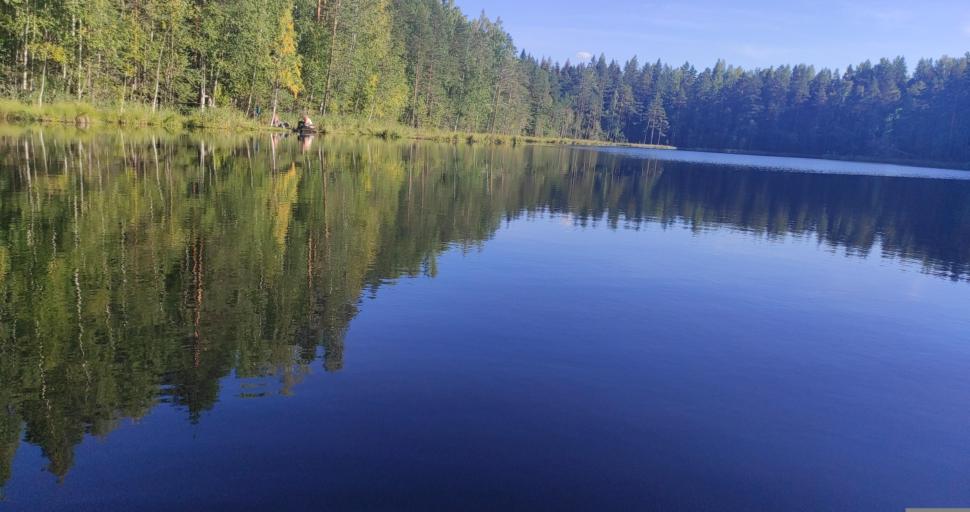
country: RU
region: St.-Petersburg
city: Komarovo
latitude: 60.2243
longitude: 29.8028
